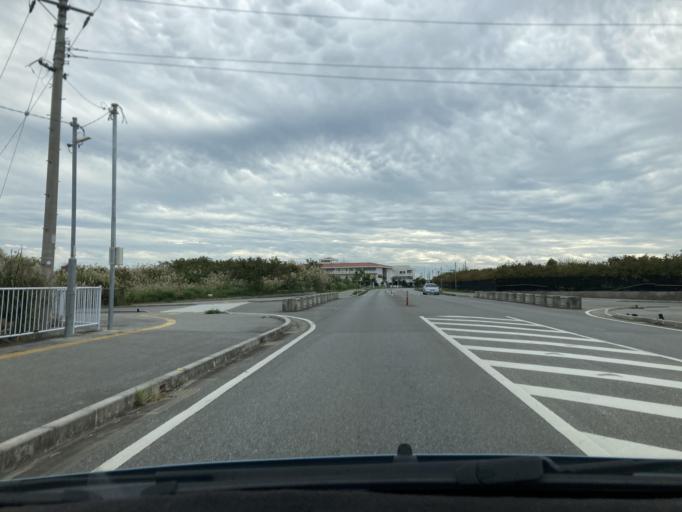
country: JP
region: Okinawa
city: Ishikawa
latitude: 26.3992
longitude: 127.7400
